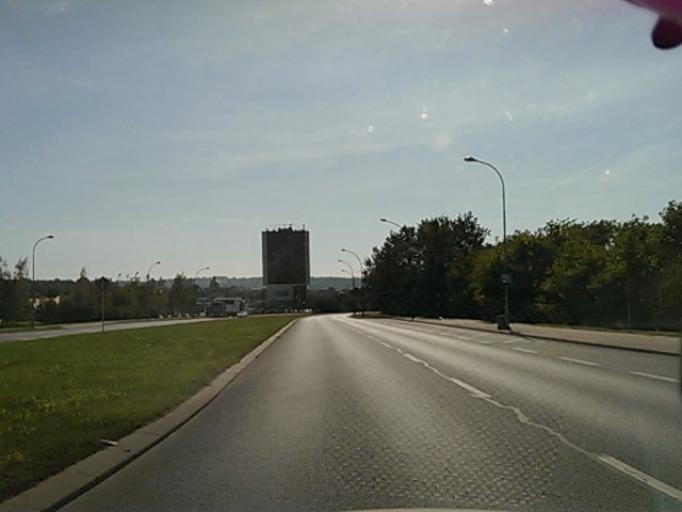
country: PL
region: Subcarpathian Voivodeship
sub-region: Rzeszow
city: Rzeszow
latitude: 50.0321
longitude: 22.0335
